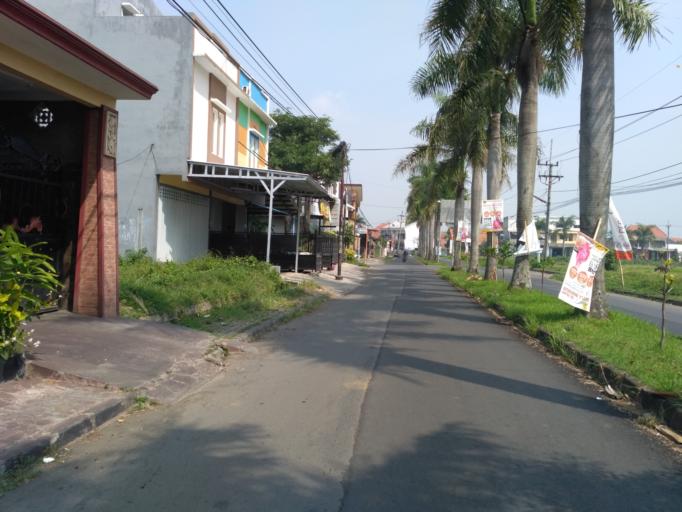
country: ID
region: East Java
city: Malang
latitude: -7.9660
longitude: 112.6671
